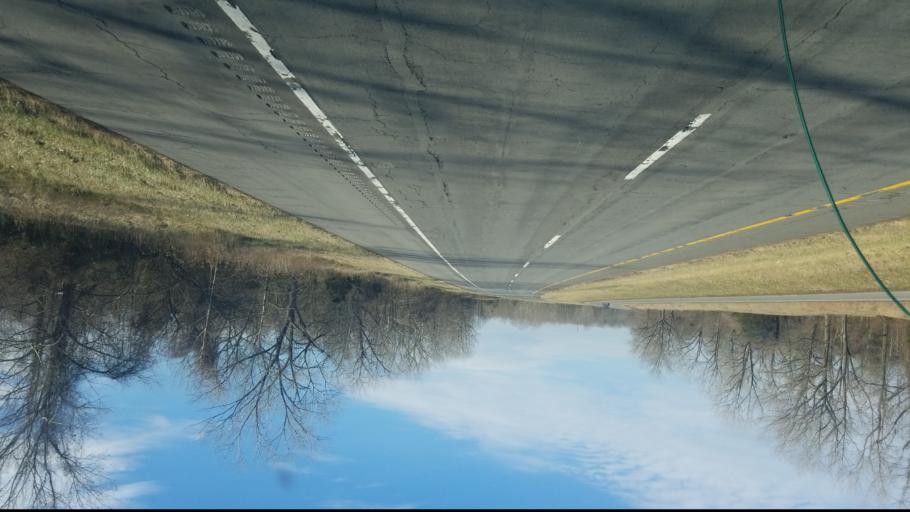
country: US
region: Illinois
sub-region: Saline County
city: Carrier Mills
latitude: 37.7308
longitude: -88.7354
